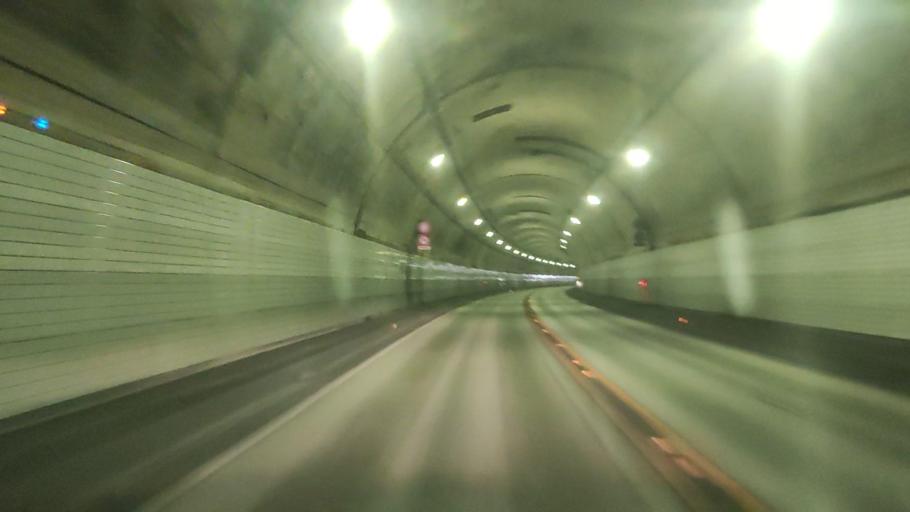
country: JP
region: Fukuoka
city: Maebaru-chuo
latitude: 33.4794
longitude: 130.2888
